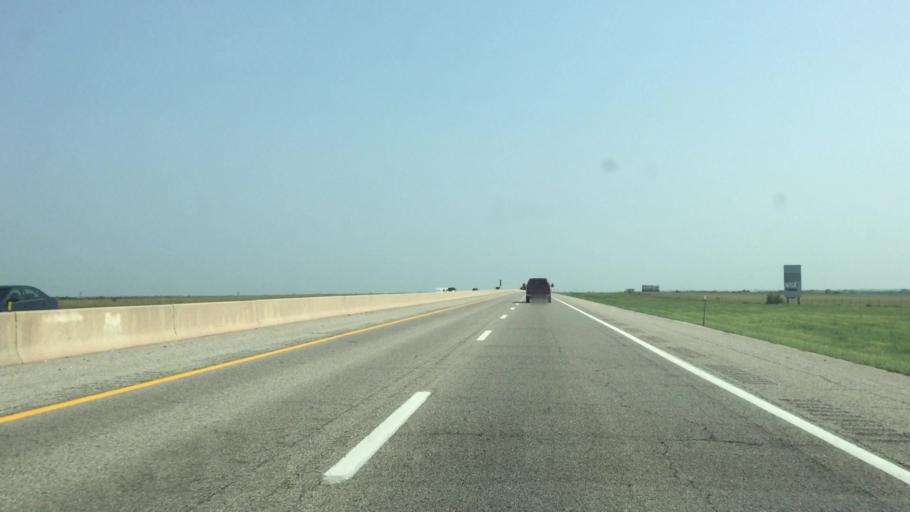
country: US
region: Kansas
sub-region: Lyon County
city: Emporia
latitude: 38.3479
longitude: -96.2904
